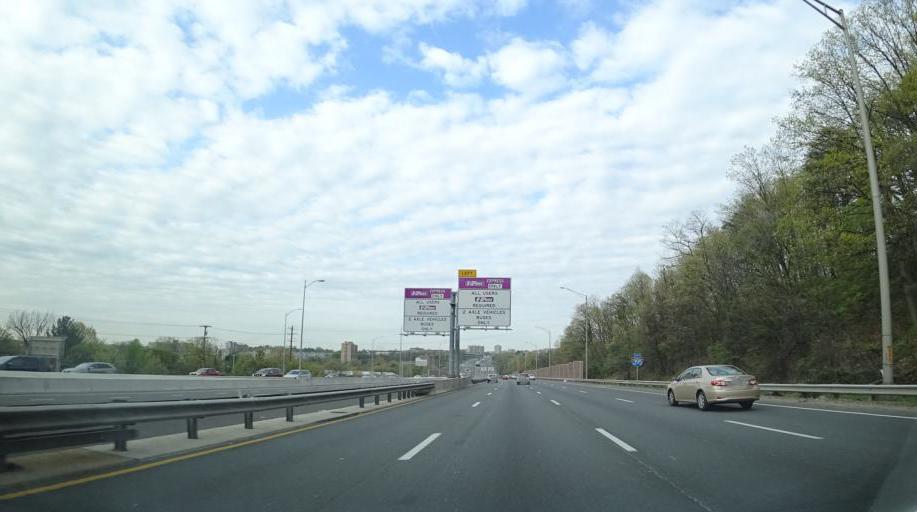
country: US
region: Virginia
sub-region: Fairfax County
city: Lincolnia
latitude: 38.8258
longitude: -77.1220
